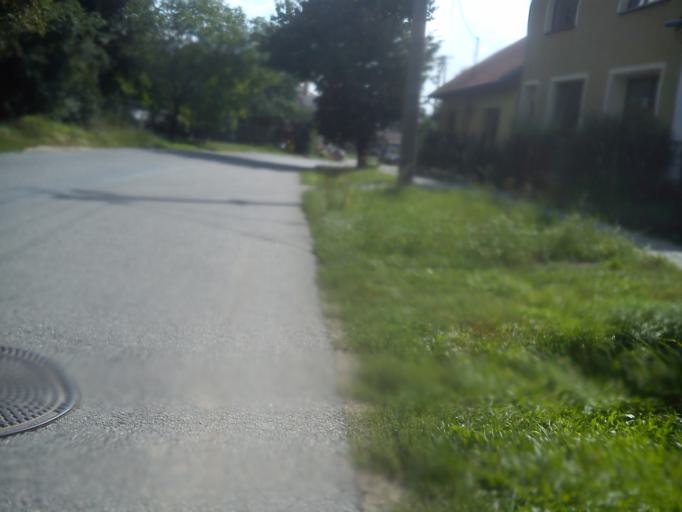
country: CZ
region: South Moravian
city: Sokolnice
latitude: 49.1098
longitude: 16.7296
